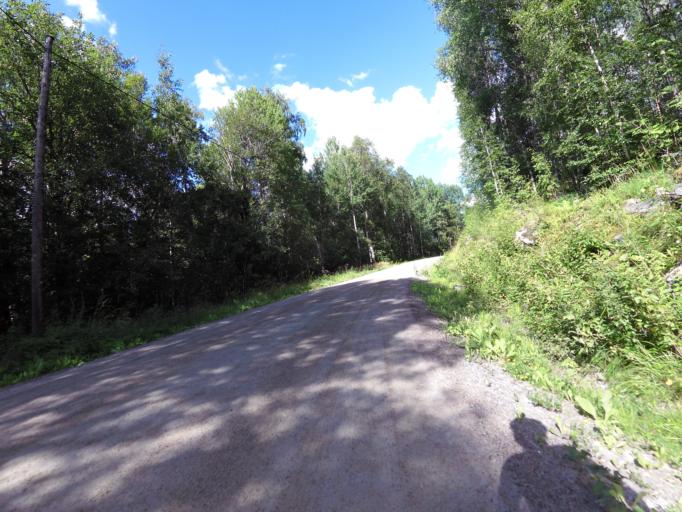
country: SE
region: Dalarna
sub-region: Faluns Kommun
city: Svardsjo
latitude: 60.6963
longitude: 15.8918
